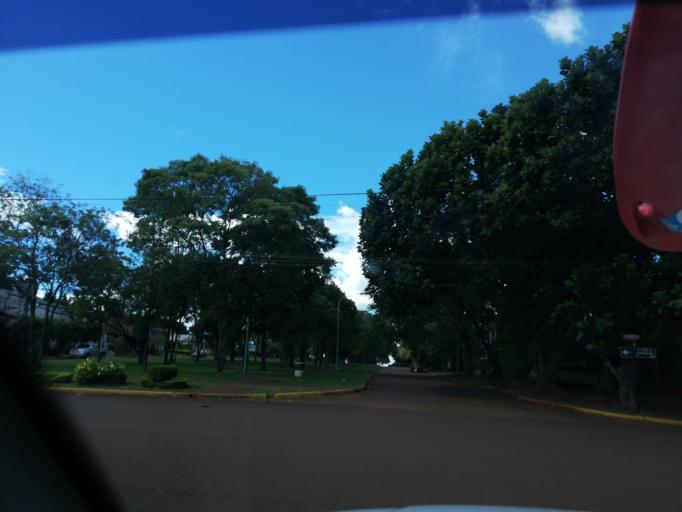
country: AR
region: Misiones
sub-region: Departamento de Apostoles
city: Apostoles
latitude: -27.9174
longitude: -55.7512
